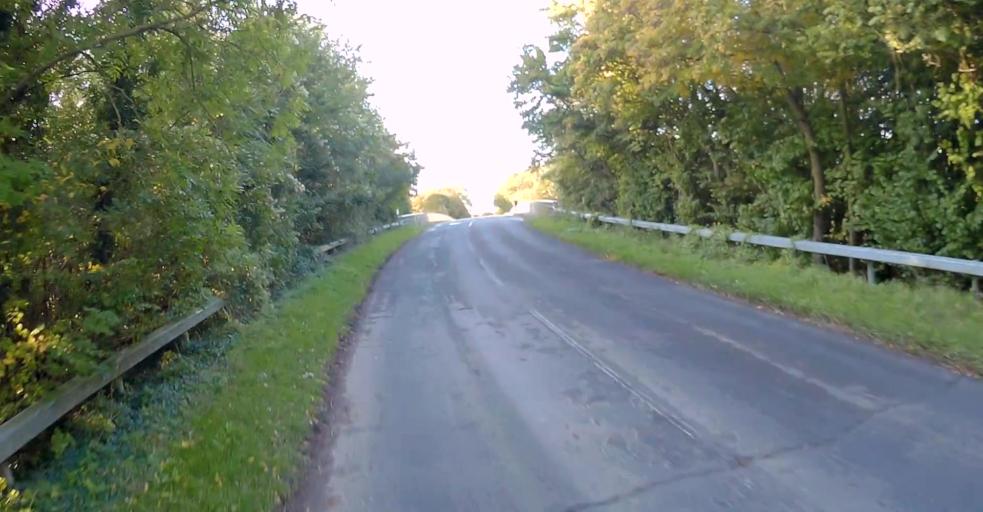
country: GB
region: England
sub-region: Hampshire
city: Old Basing
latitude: 51.2635
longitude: -1.0254
